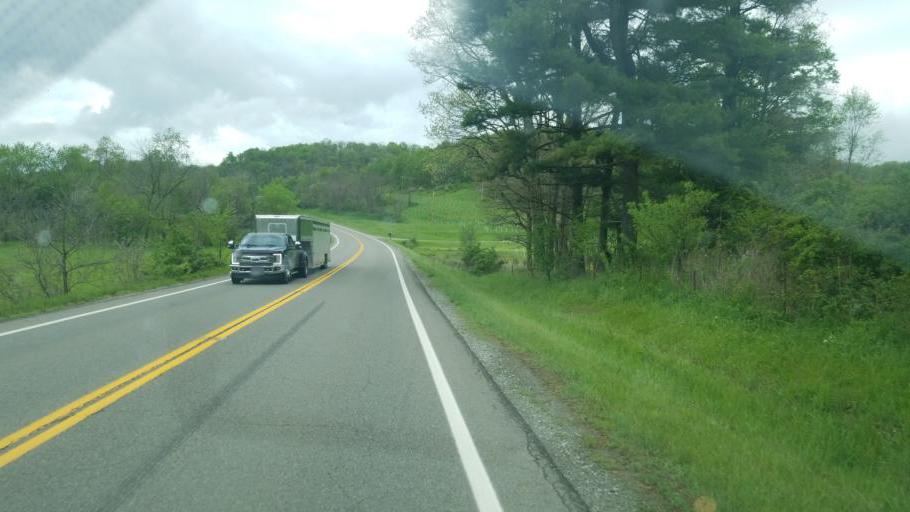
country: US
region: Ohio
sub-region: Harrison County
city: Cadiz
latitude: 40.2923
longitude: -81.0575
